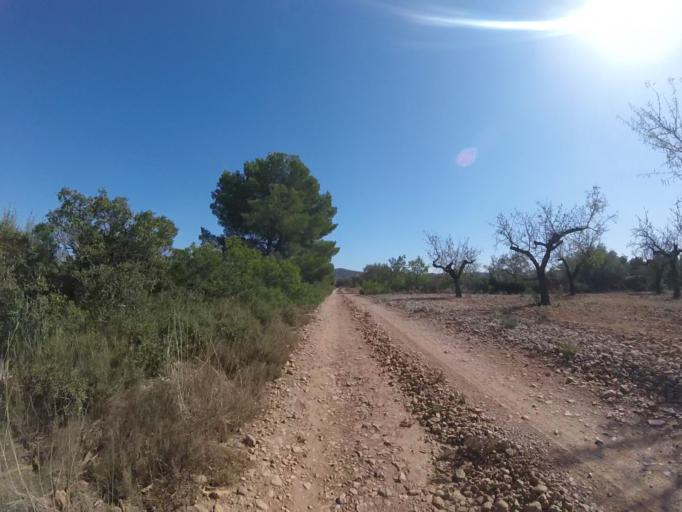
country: ES
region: Valencia
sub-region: Provincia de Castello
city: Cuevas de Vinroma
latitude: 40.2811
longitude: 0.0843
